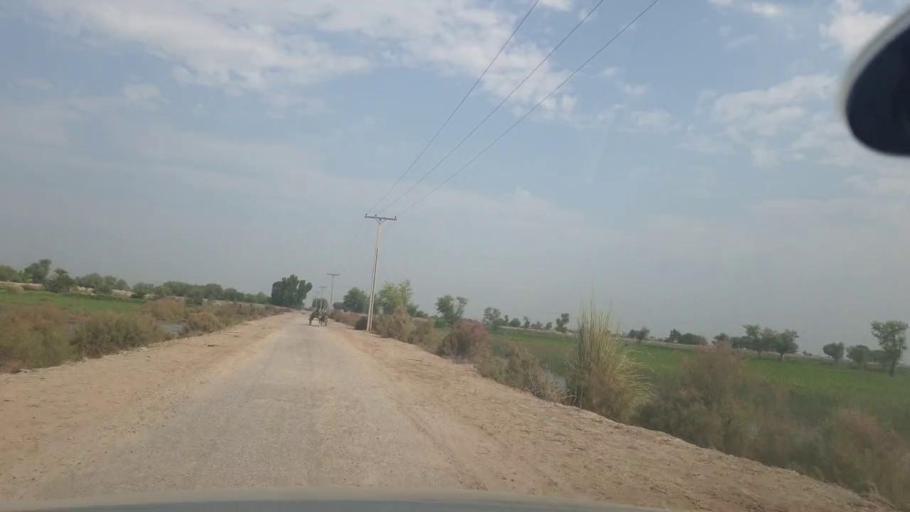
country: PK
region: Balochistan
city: Mehrabpur
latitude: 28.0594
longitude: 68.1054
